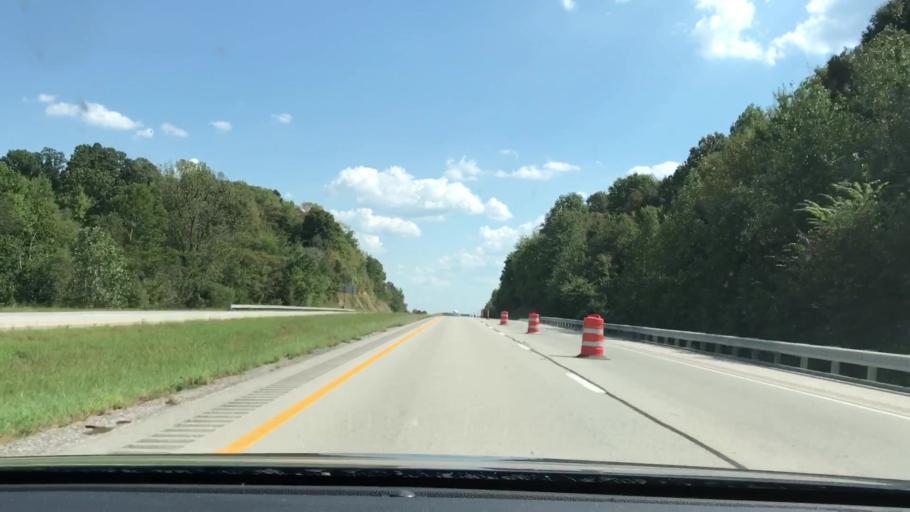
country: US
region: Kentucky
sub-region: Butler County
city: Morgantown
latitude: 37.2276
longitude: -86.7229
